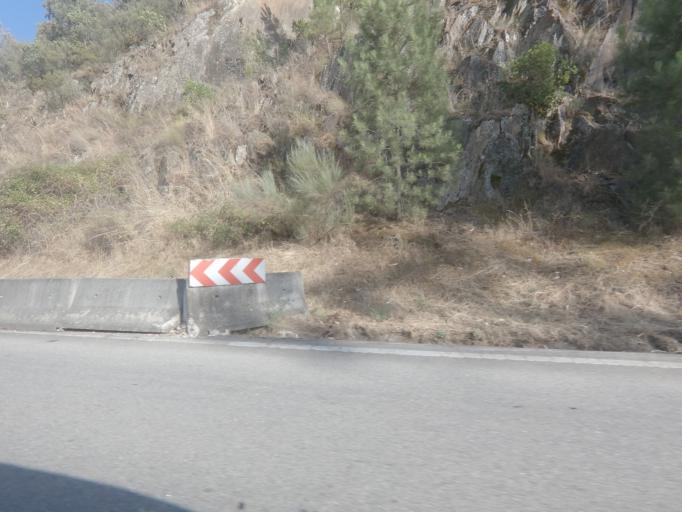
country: PT
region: Viseu
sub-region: Tabuaco
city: Tabuaco
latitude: 41.1554
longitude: -7.5883
